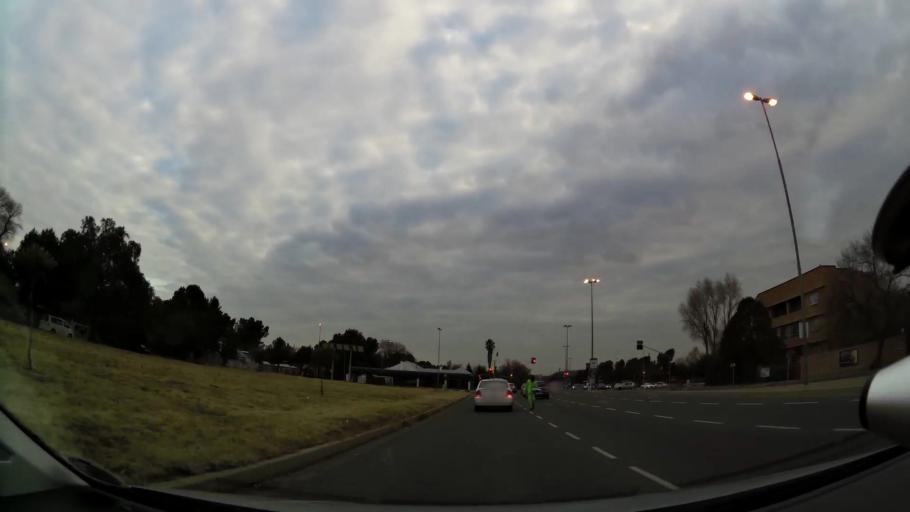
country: ZA
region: Orange Free State
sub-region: Mangaung Metropolitan Municipality
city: Bloemfontein
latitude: -29.1219
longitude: 26.1984
